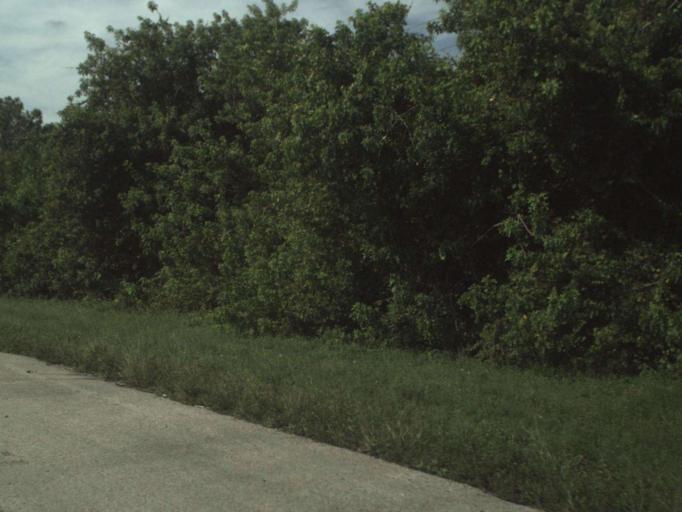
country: US
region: Florida
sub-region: Indian River County
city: West Vero Corridor
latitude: 27.6674
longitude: -80.5298
